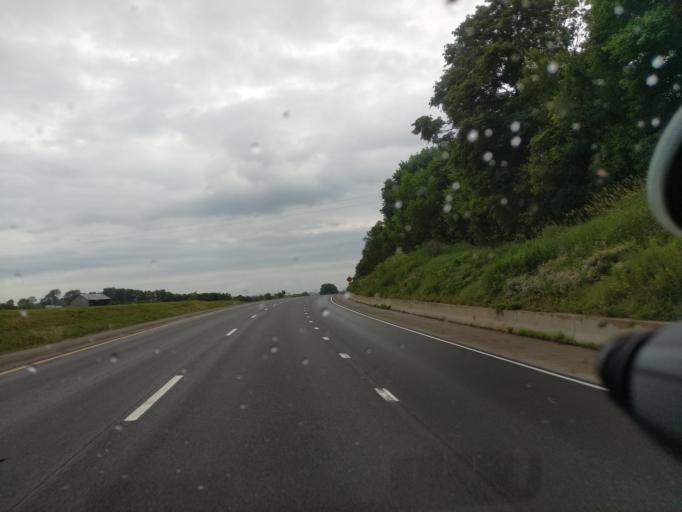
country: US
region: Pennsylvania
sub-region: Northumberland County
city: Milton
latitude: 41.0252
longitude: -76.8005
